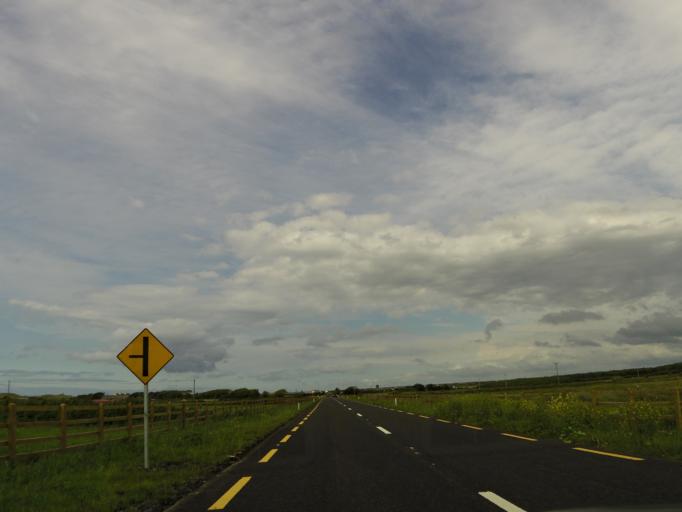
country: IE
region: Munster
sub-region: An Clar
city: Kilrush
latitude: 52.7415
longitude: -9.4813
